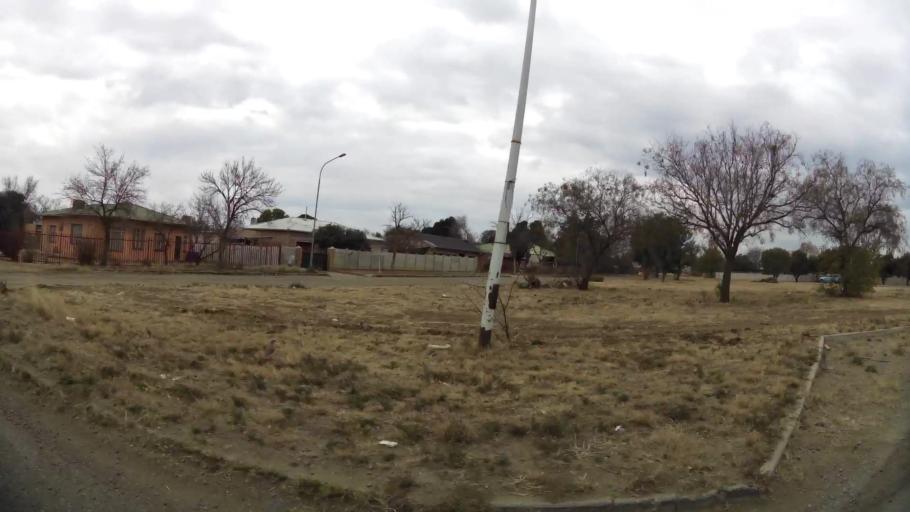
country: ZA
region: Orange Free State
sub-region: Fezile Dabi District Municipality
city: Kroonstad
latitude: -27.6787
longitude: 27.2335
